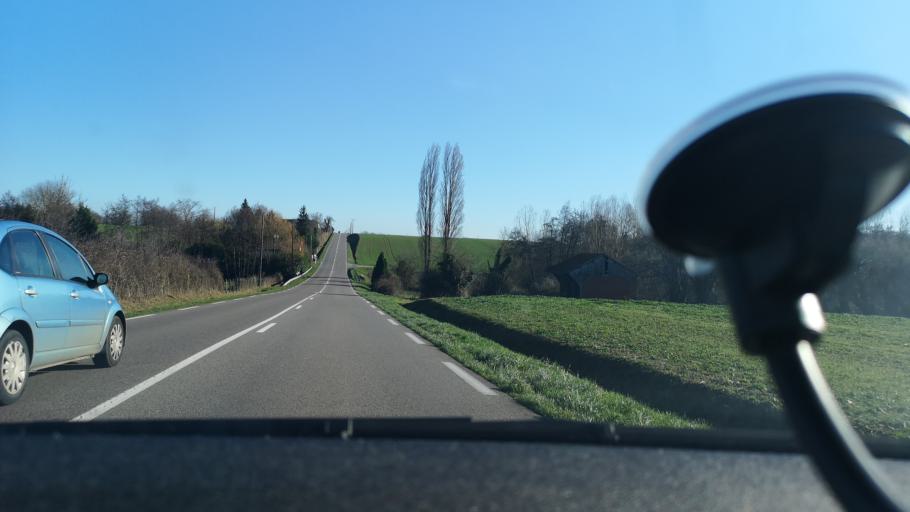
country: FR
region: Bourgogne
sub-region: Departement de Saone-et-Loire
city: Saint-Martin-en-Bresse
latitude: 46.7493
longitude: 5.0422
